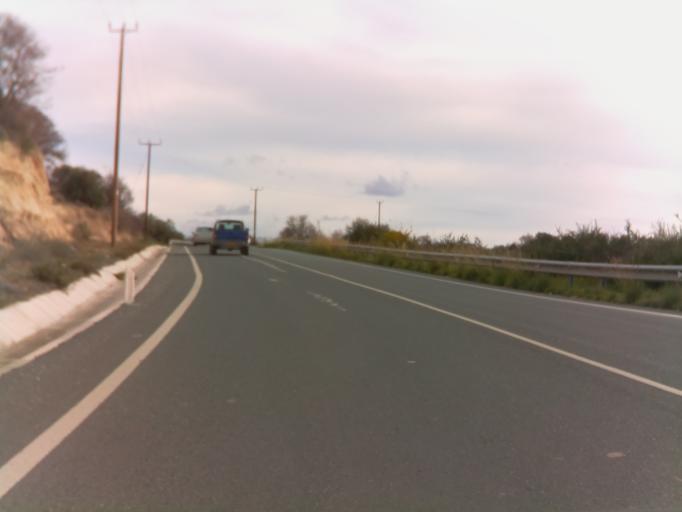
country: CY
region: Pafos
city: Polis
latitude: 34.9923
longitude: 32.4049
